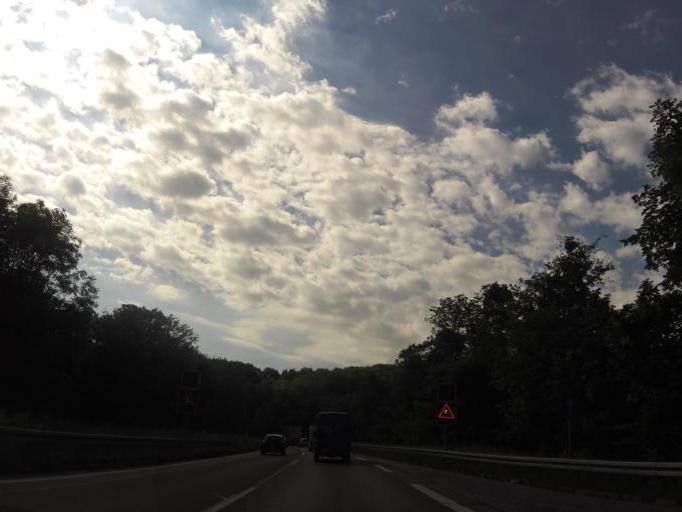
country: DE
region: Baden-Wuerttemberg
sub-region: Regierungsbezirk Stuttgart
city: Wiesensteig
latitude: 48.5524
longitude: 9.6329
